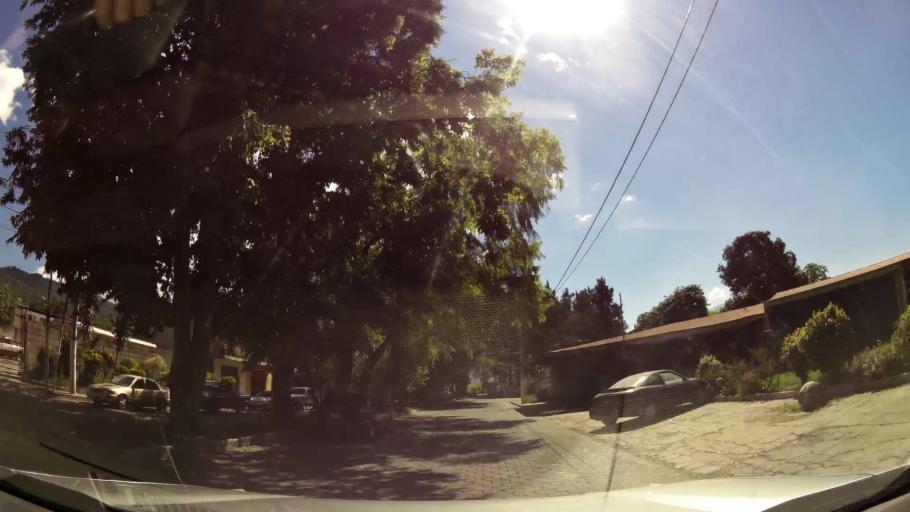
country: GT
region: Guatemala
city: Villa Canales
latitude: 14.4778
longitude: -90.5351
